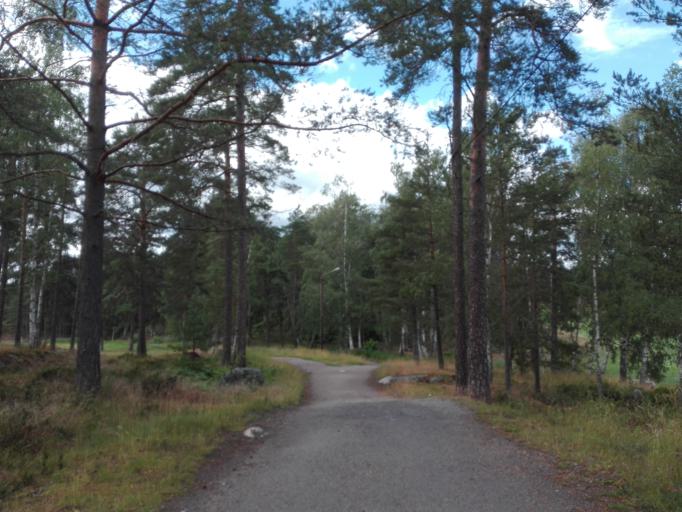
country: SE
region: Stockholm
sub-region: Nacka Kommun
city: Fisksatra
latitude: 59.2838
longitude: 18.2647
